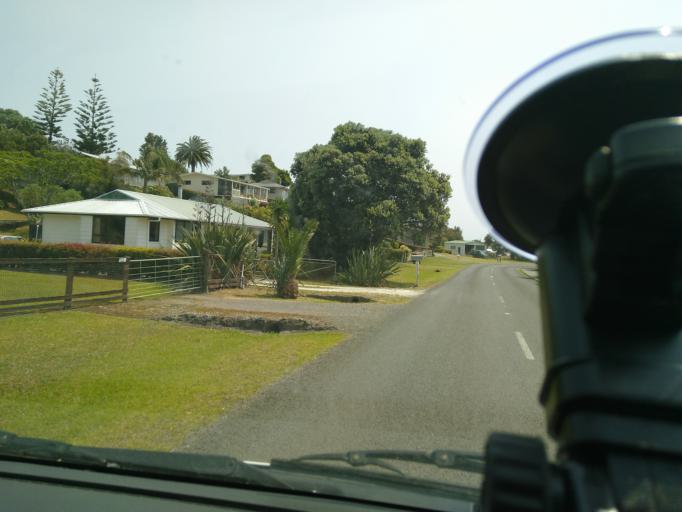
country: NZ
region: Northland
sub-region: Far North District
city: Kaitaia
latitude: -34.8167
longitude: 173.1163
